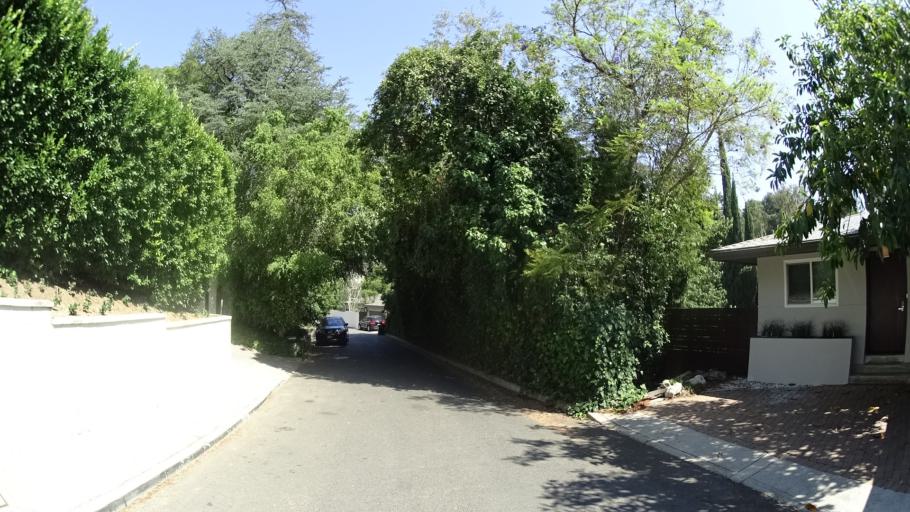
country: US
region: California
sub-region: Los Angeles County
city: North Hollywood
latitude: 34.1387
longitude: -118.3899
